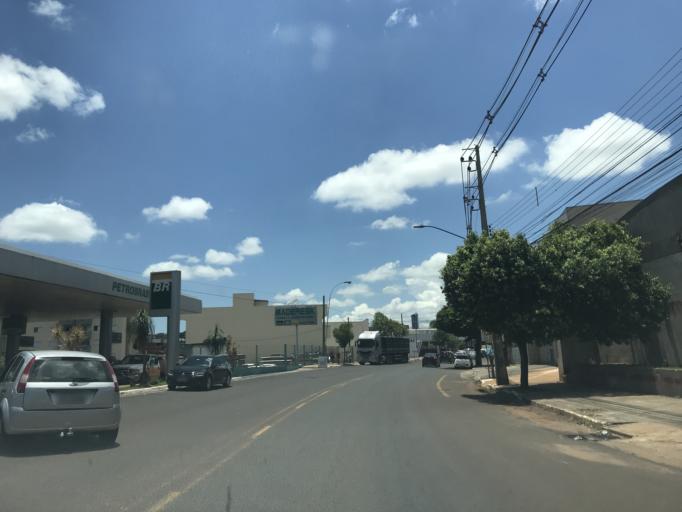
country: BR
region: Parana
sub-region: Marialva
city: Marialva
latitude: -23.4797
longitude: -51.8040
